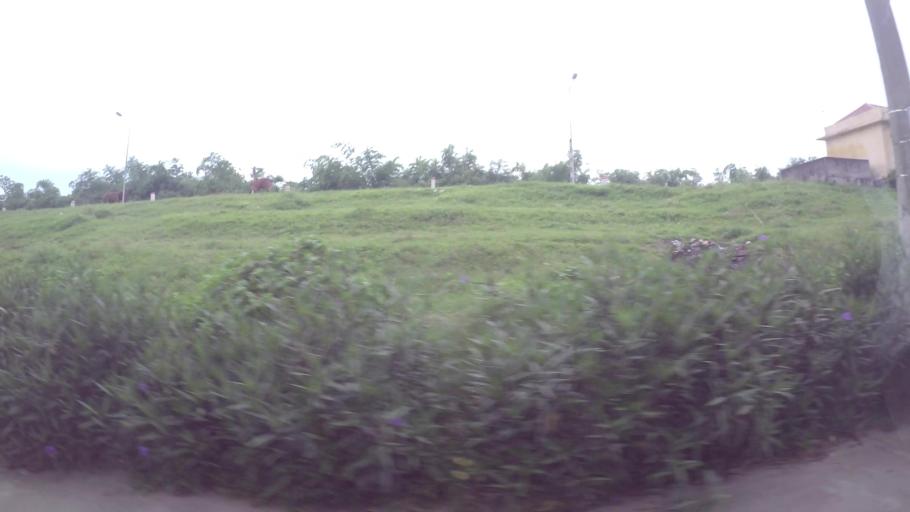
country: VN
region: Ha Noi
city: Trau Quy
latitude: 21.0452
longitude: 105.9291
